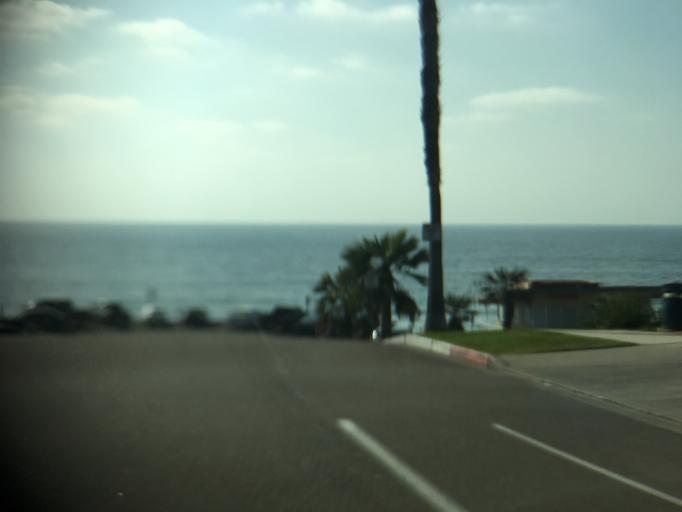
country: US
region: California
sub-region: San Diego County
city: Encinitas
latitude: 33.0471
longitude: -117.2967
